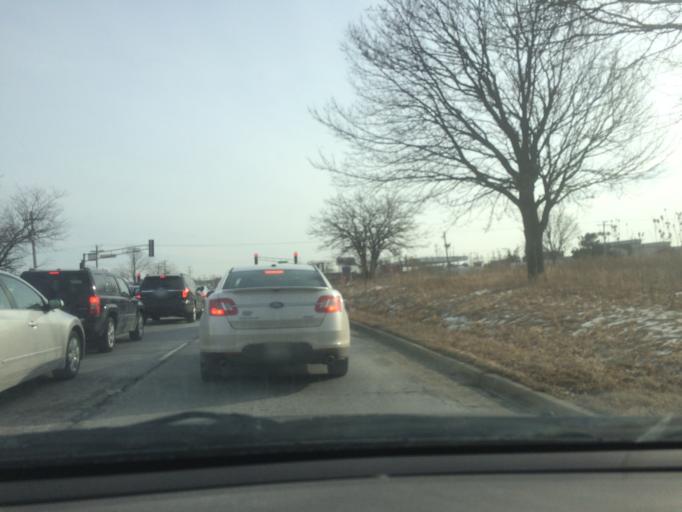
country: US
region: Illinois
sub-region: Cook County
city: Streamwood
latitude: 42.0464
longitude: -88.1458
